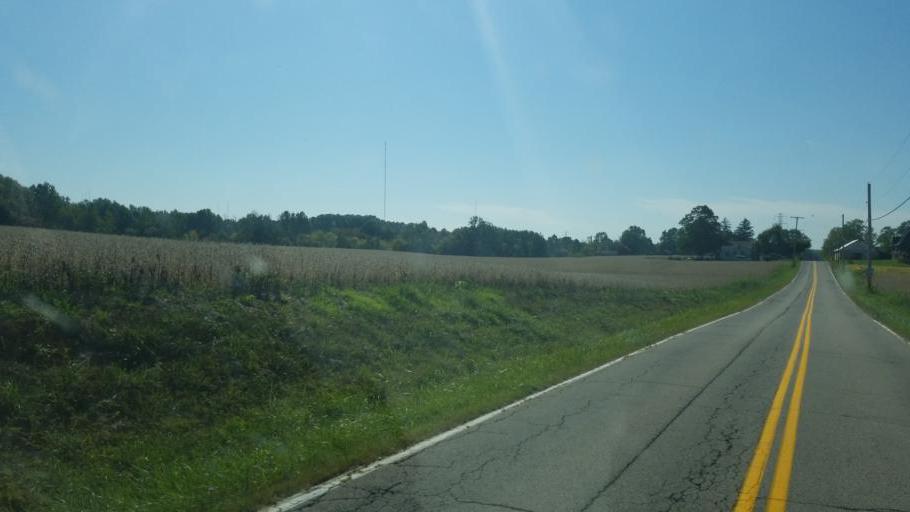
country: US
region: Ohio
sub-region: Richland County
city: Ontario
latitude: 40.7711
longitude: -82.6240
